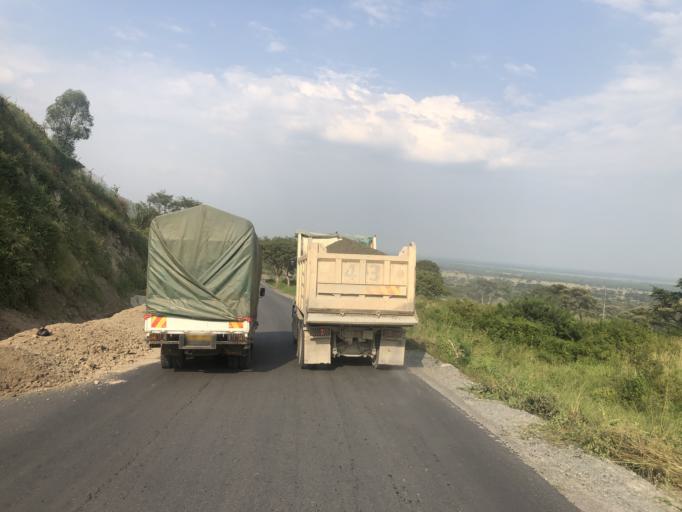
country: UG
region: Western Region
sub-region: Rubirizi District
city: Rubirizi
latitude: -0.2150
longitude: 30.0946
